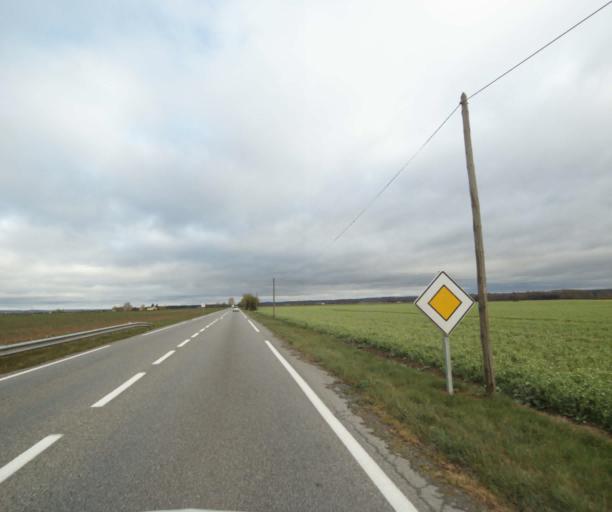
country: FR
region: Midi-Pyrenees
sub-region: Departement de l'Ariege
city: Saverdun
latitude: 43.2549
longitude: 1.5638
